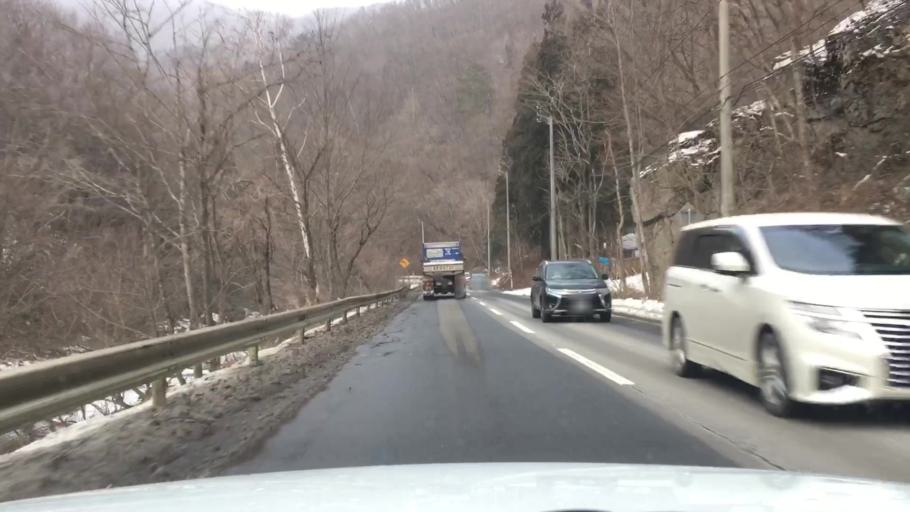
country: JP
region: Iwate
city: Tono
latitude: 39.6200
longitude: 141.4758
